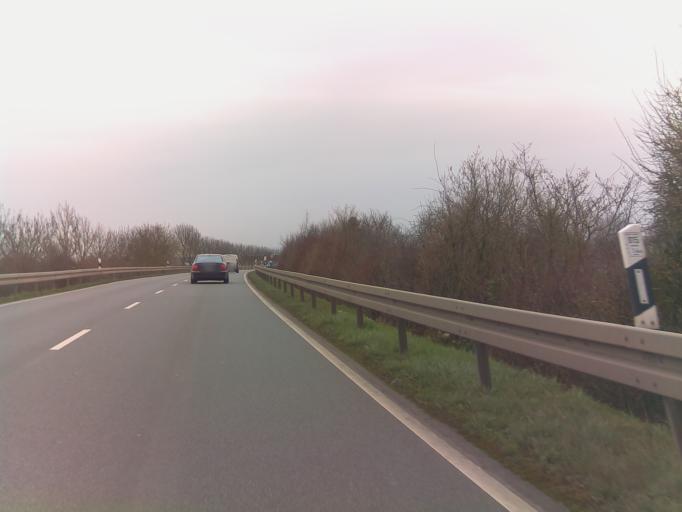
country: DE
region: Hesse
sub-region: Regierungsbezirk Darmstadt
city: Stockstadt am Rhein
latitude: 49.7943
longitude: 8.4843
